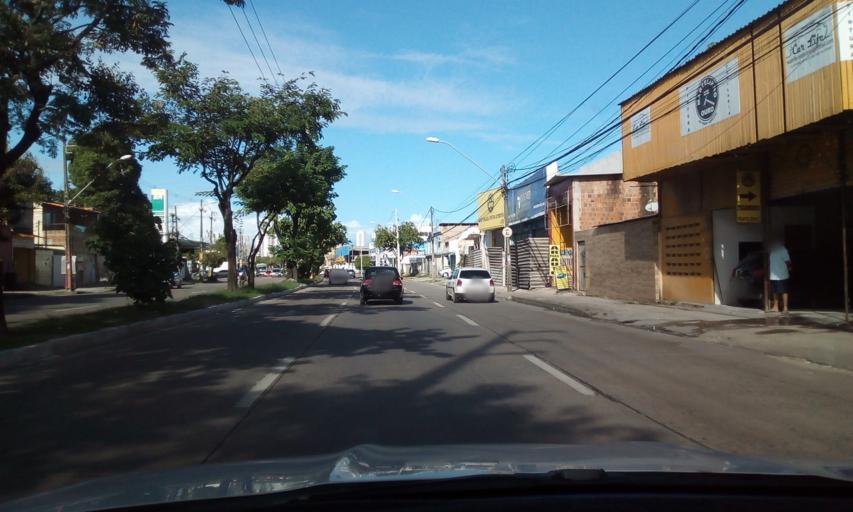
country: BR
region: Pernambuco
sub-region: Recife
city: Recife
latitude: -8.0623
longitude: -34.9189
